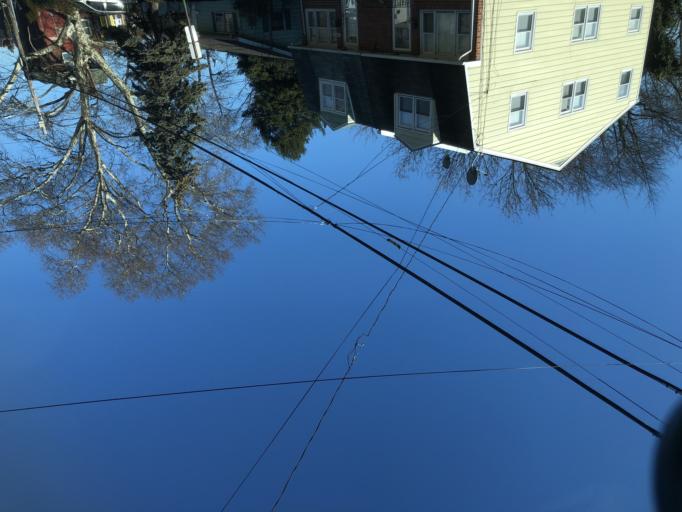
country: US
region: Pennsylvania
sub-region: Delaware County
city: Millbourne
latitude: 39.9538
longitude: -75.2541
